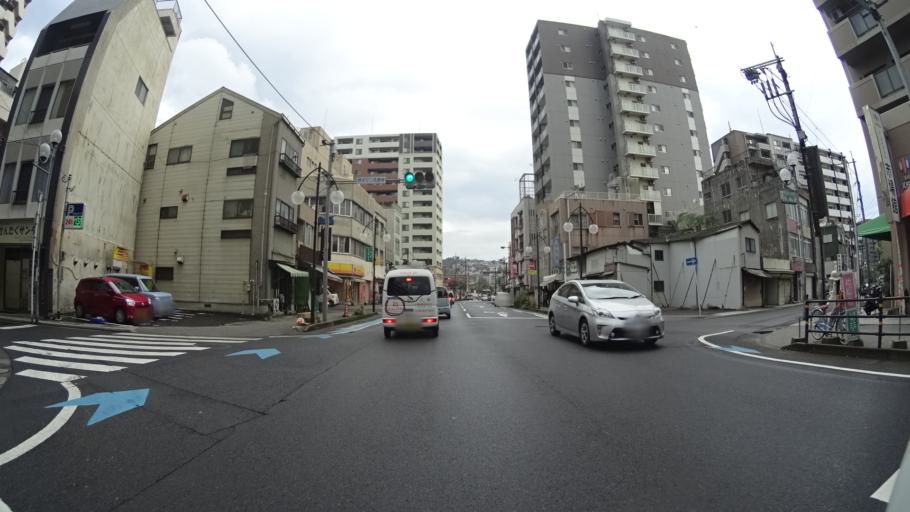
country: JP
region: Kagoshima
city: Kagoshima-shi
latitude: 31.5993
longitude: 130.5614
